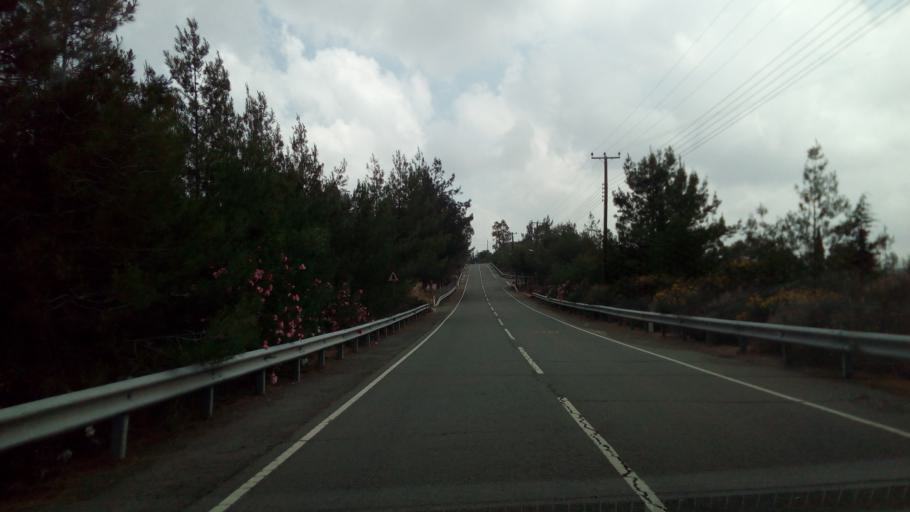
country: CY
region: Limassol
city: Pyrgos
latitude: 34.8663
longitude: 33.1948
